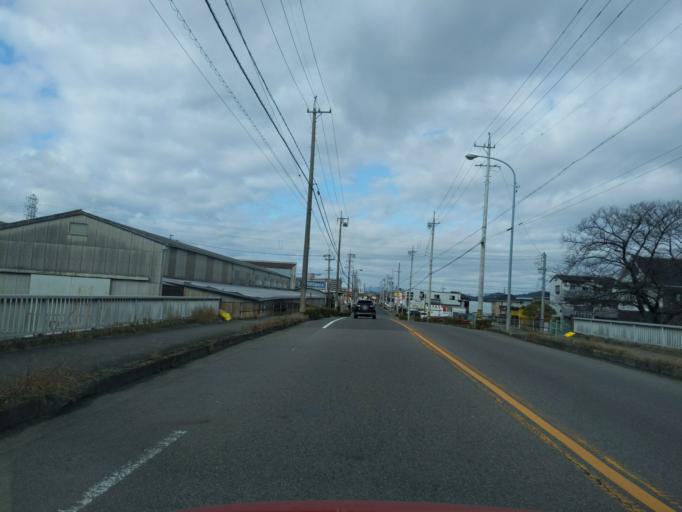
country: JP
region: Aichi
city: Kasugai
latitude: 35.2621
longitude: 136.9731
